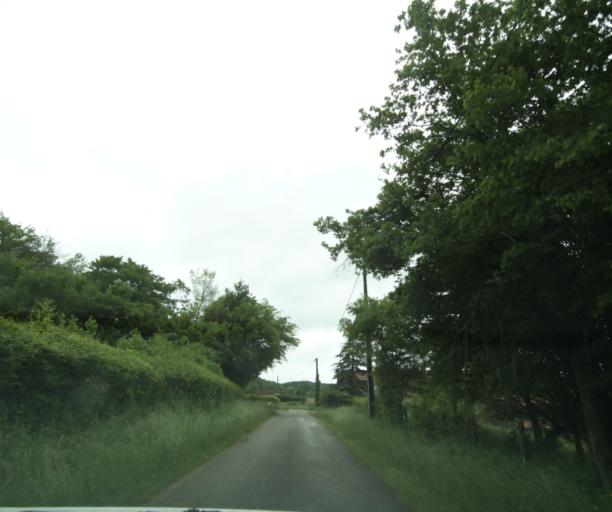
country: FR
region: Bourgogne
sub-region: Departement de Saone-et-Loire
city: Charolles
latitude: 46.5021
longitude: 4.2899
